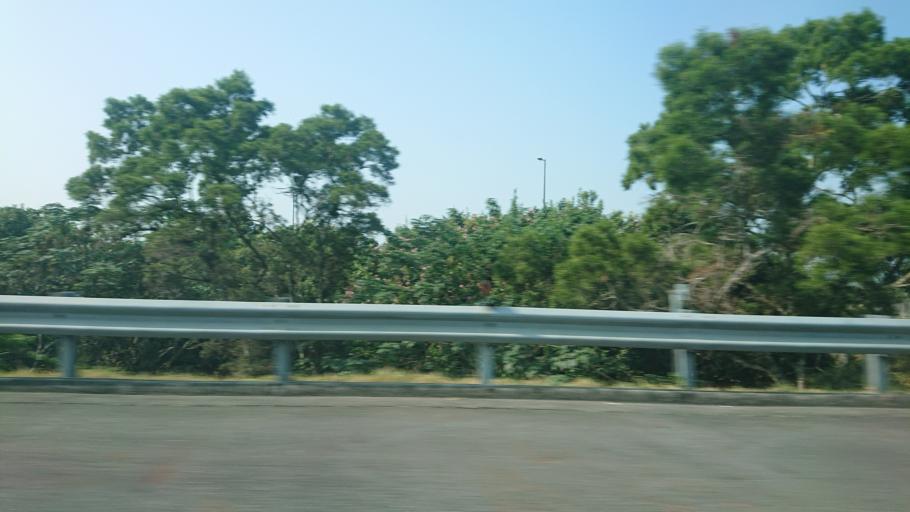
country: TW
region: Taiwan
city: Lugu
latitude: 23.7982
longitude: 120.7007
